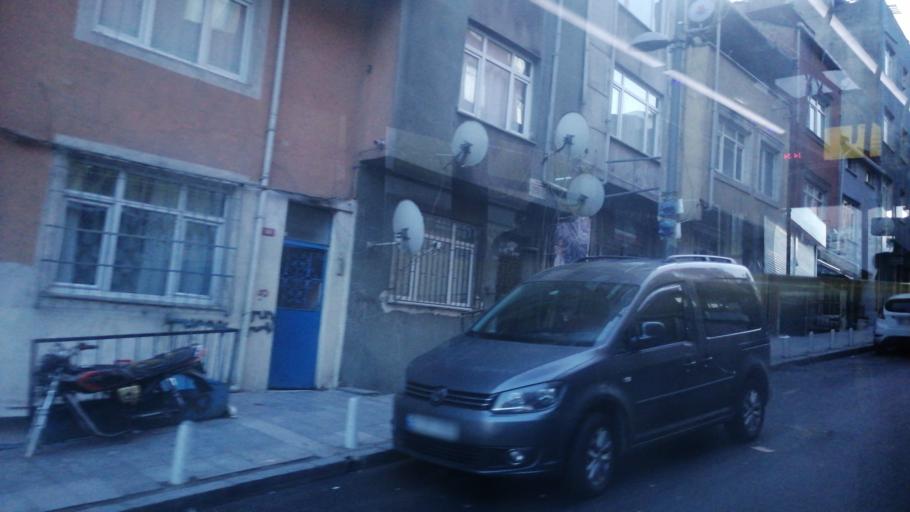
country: TR
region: Istanbul
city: Sisli
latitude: 41.0866
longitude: 28.9858
